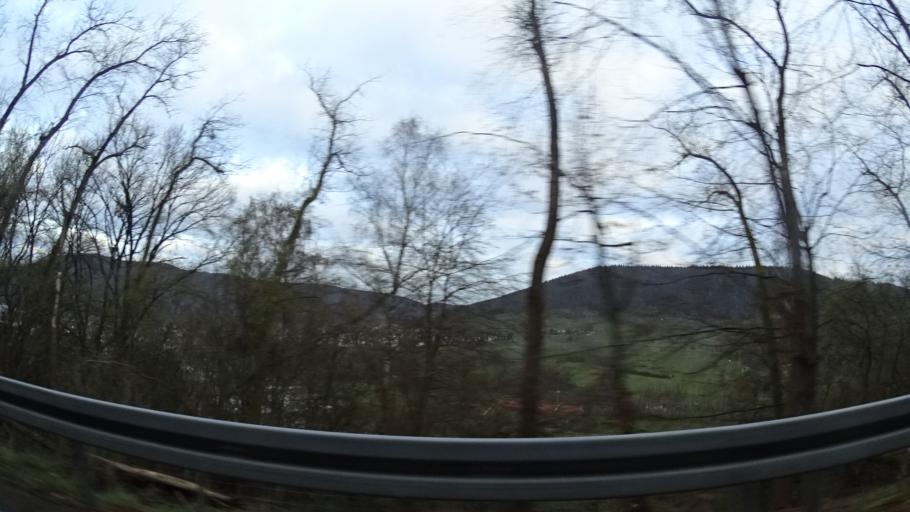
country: DE
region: Bavaria
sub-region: Regierungsbezirk Unterfranken
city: Miltenberg
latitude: 49.7014
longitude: 9.2821
